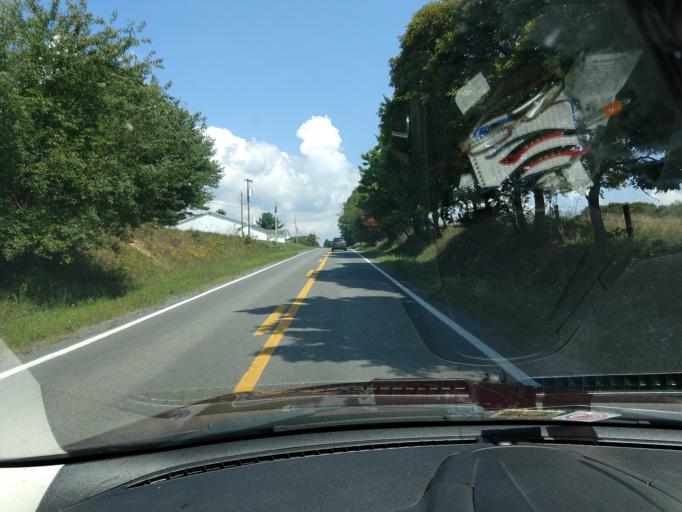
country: US
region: West Virginia
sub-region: Greenbrier County
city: Lewisburg
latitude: 37.8478
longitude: -80.5507
